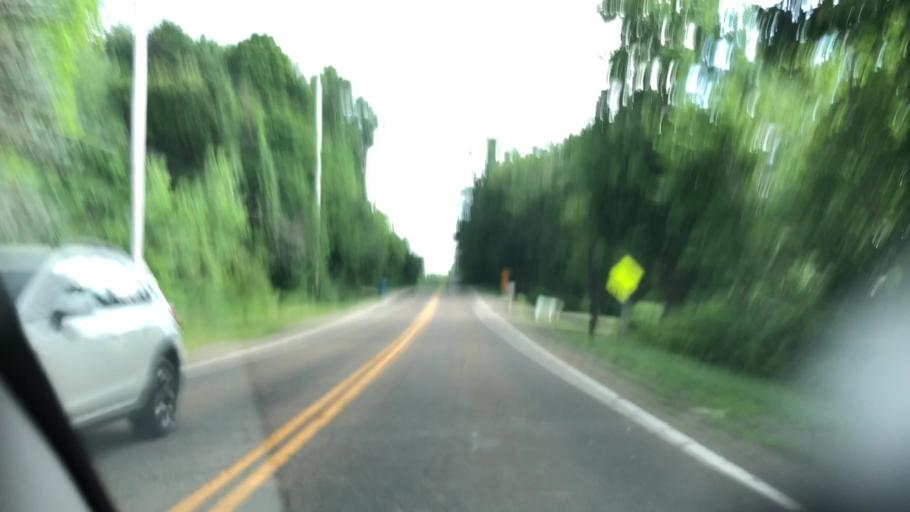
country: US
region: Ohio
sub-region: Summit County
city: Fairlawn
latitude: 41.0867
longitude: -81.6446
